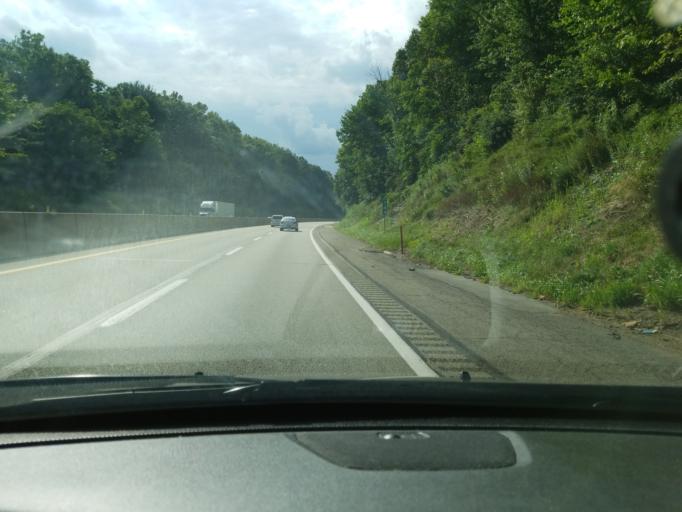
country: US
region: Pennsylvania
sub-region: Beaver County
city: West Mayfield
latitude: 40.7986
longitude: -80.2914
